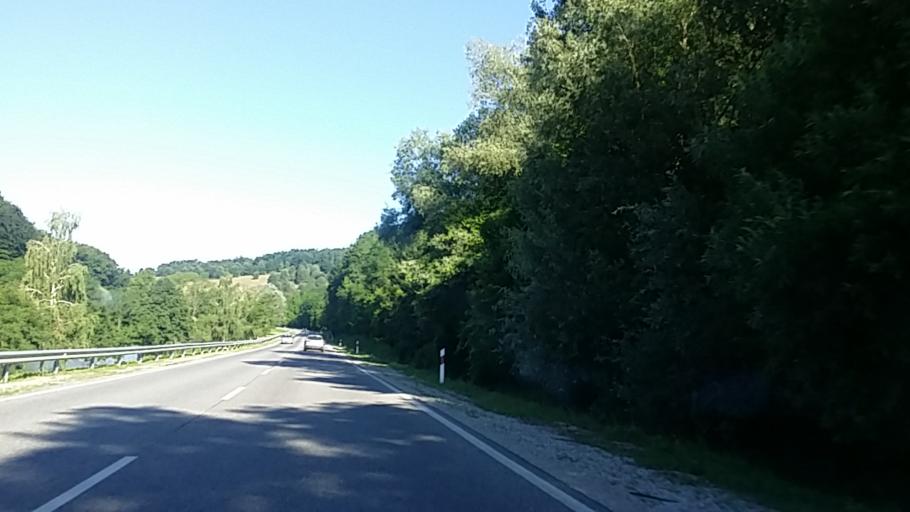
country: HU
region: Zala
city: Heviz
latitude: 46.8073
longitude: 17.0853
